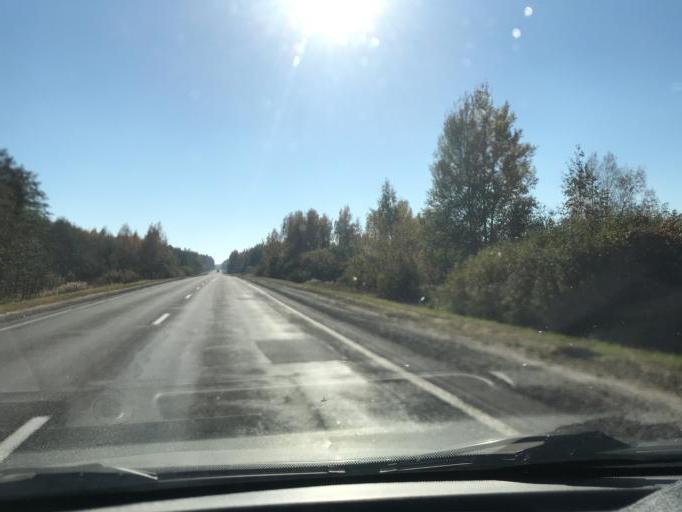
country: BY
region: Gomel
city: Kastsyukowka
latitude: 52.4413
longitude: 30.8255
